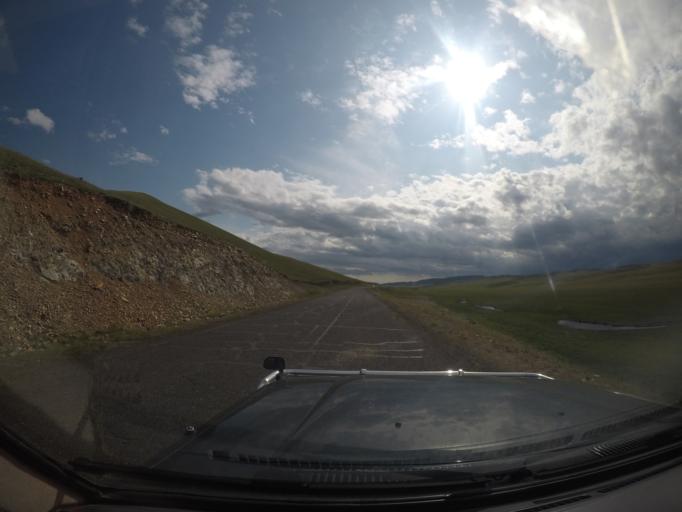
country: MN
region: Hentiy
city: Modot
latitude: 47.7644
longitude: 108.6420
